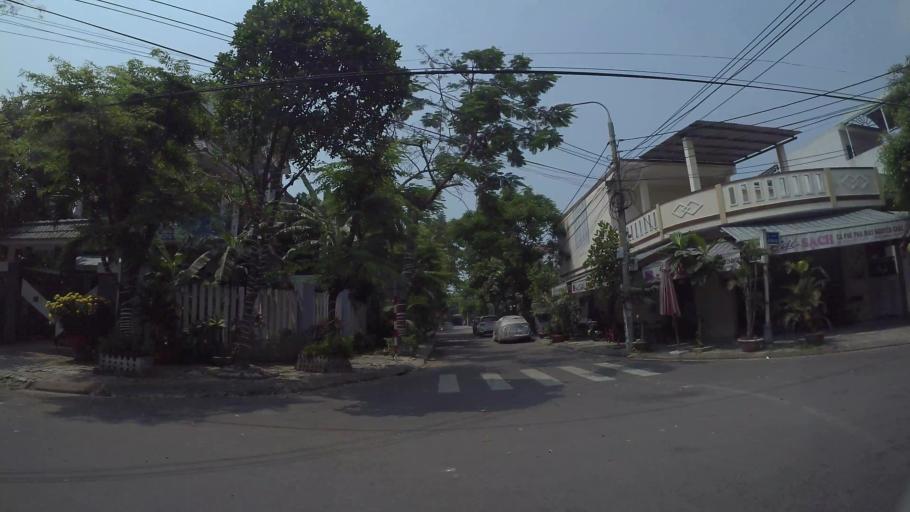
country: VN
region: Da Nang
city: Cam Le
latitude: 16.0040
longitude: 108.2171
